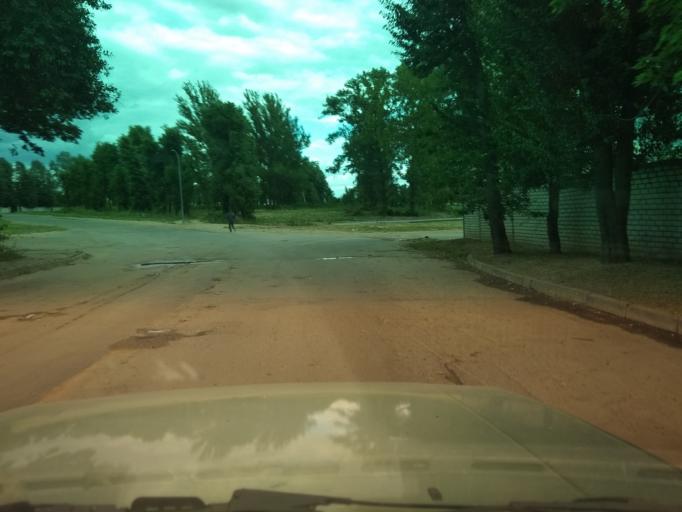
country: BY
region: Mogilev
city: Mahilyow
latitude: 53.9240
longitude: 30.3541
